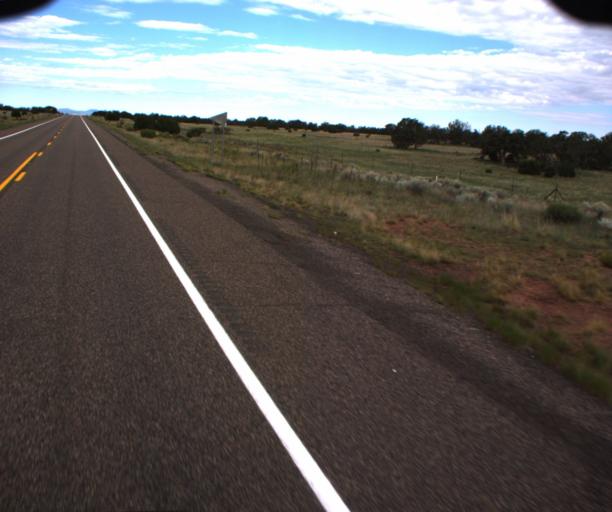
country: US
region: Arizona
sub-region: Apache County
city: Springerville
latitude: 34.1606
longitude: -109.0876
